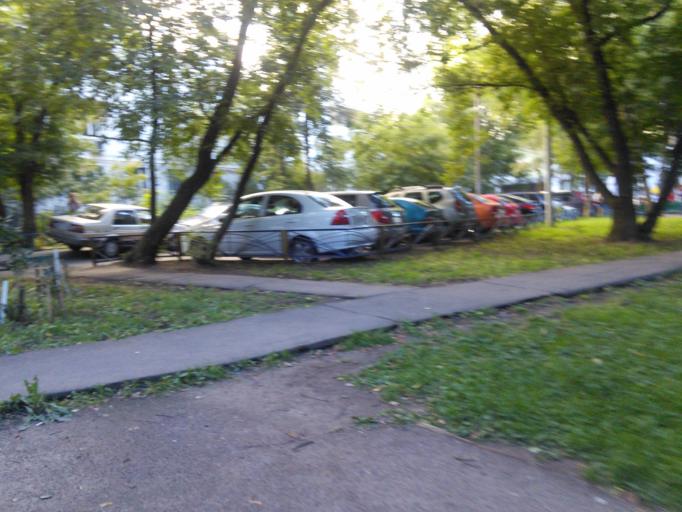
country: RU
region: Moskovskaya
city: Levoberezhnyy
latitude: 55.8468
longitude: 37.4448
